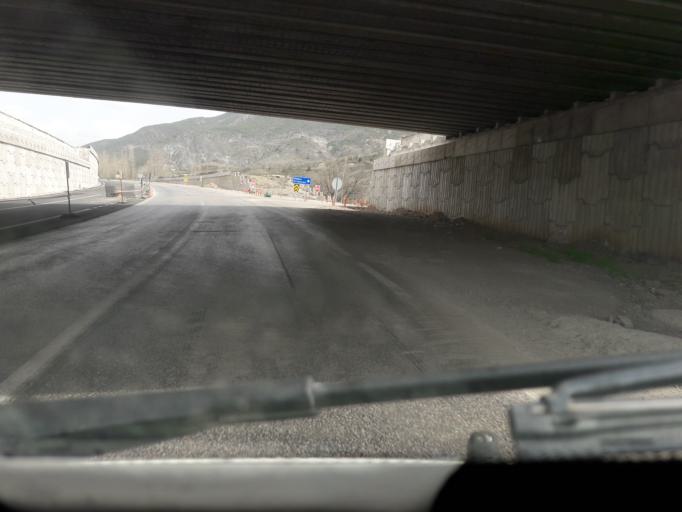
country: TR
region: Gumushane
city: Kale
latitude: 40.4059
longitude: 39.6073
